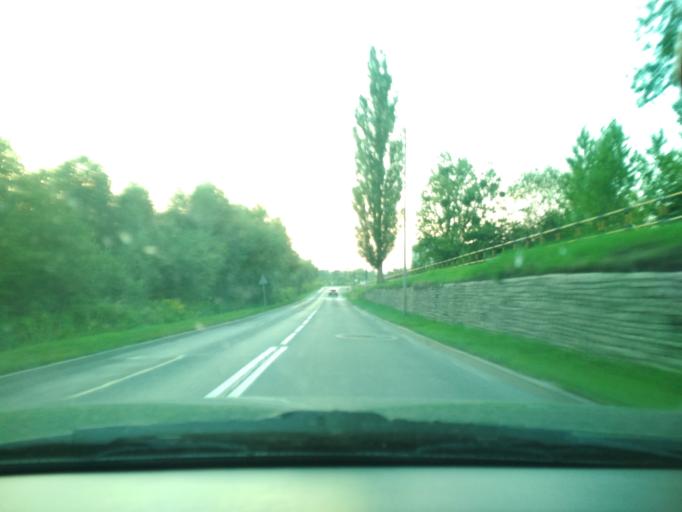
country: PL
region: Silesian Voivodeship
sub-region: Gliwice
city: Gliwice
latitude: 50.2724
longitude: 18.6848
